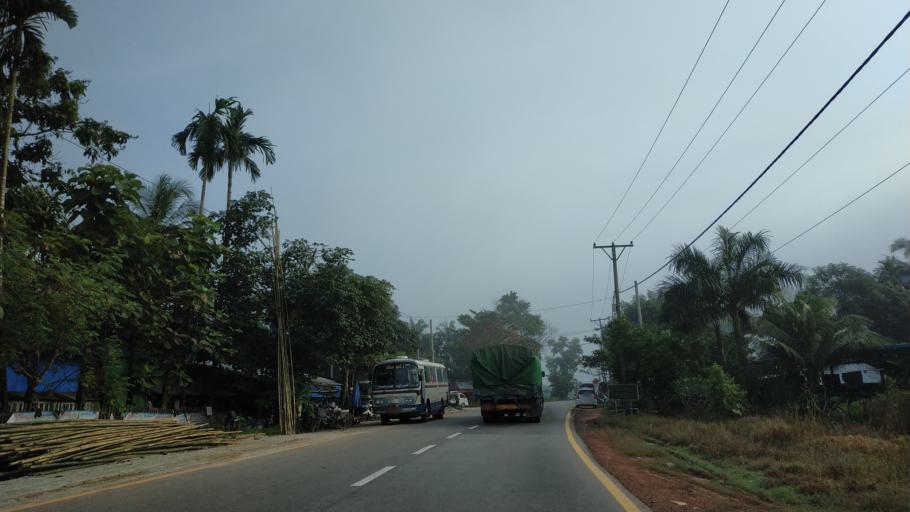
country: MM
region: Tanintharyi
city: Dawei
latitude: 14.1993
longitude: 98.2022
